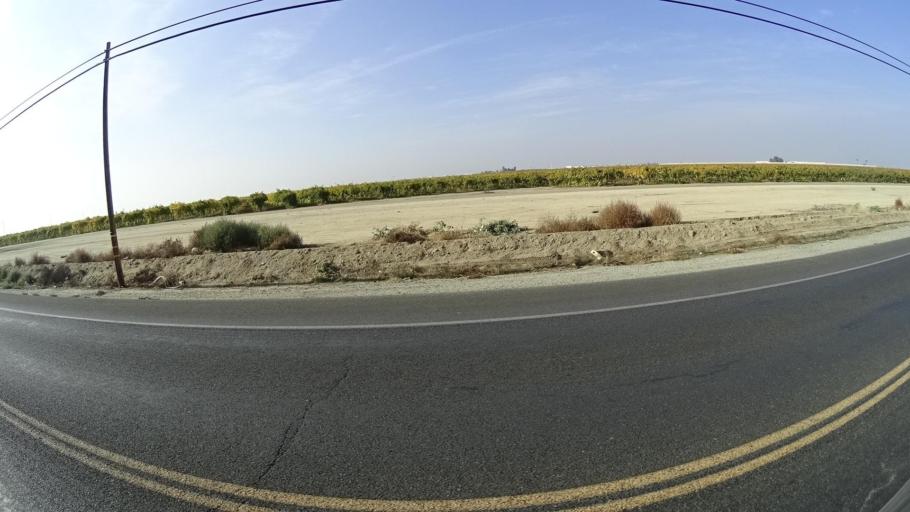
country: US
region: California
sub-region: Tulare County
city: Richgrove
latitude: 35.7887
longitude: -119.1159
